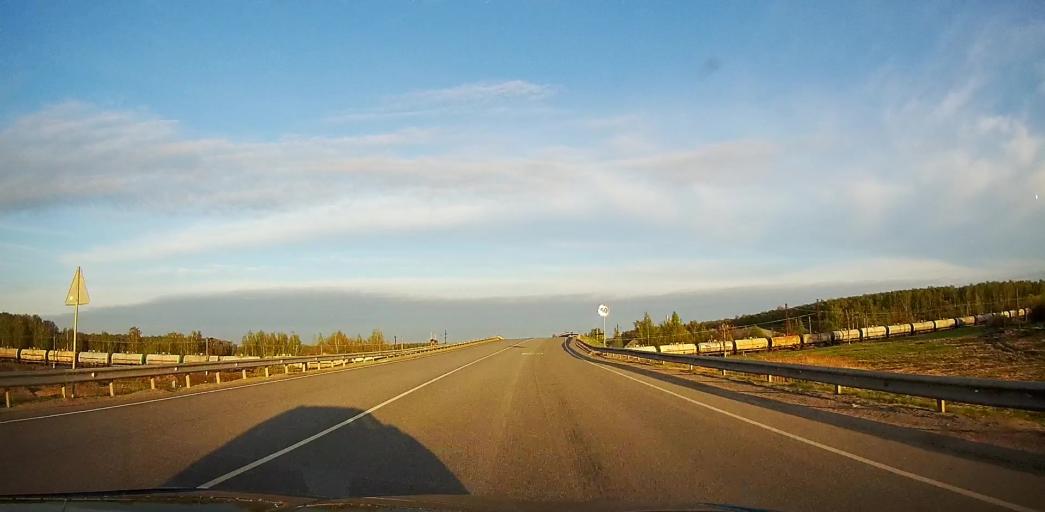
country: RU
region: Moskovskaya
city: Troitskoye
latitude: 55.2186
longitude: 38.5866
